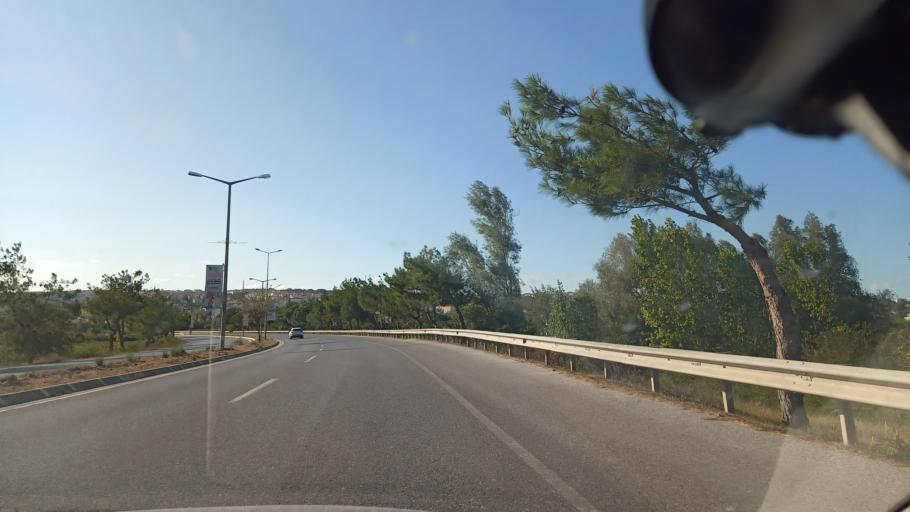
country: TR
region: Sakarya
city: Kazimpasa
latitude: 40.8478
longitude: 30.3247
